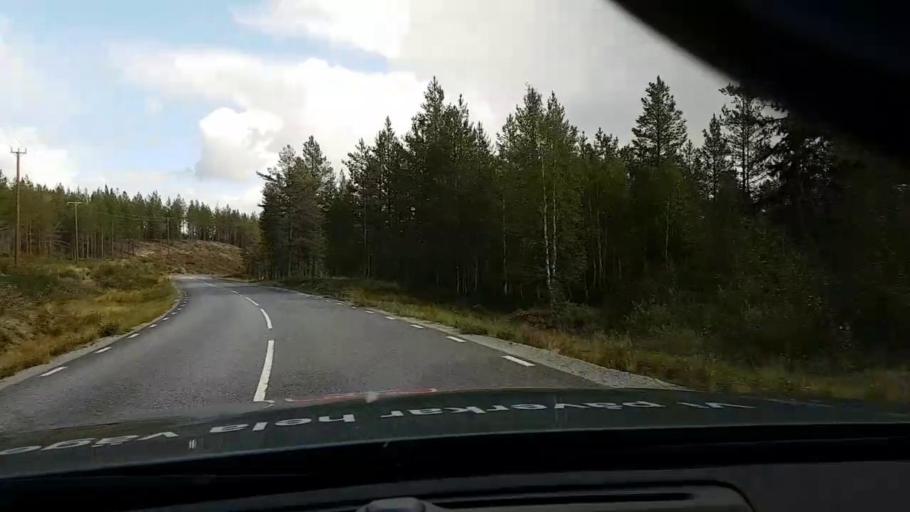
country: SE
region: Vaesterbotten
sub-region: Asele Kommun
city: Asele
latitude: 63.8495
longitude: 17.3990
